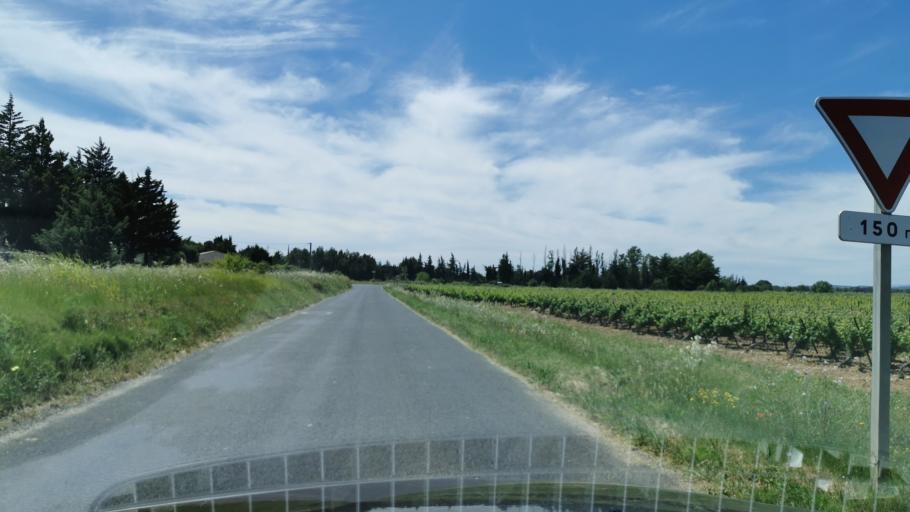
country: FR
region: Languedoc-Roussillon
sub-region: Departement de l'Aude
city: Nevian
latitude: 43.2154
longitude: 2.9145
